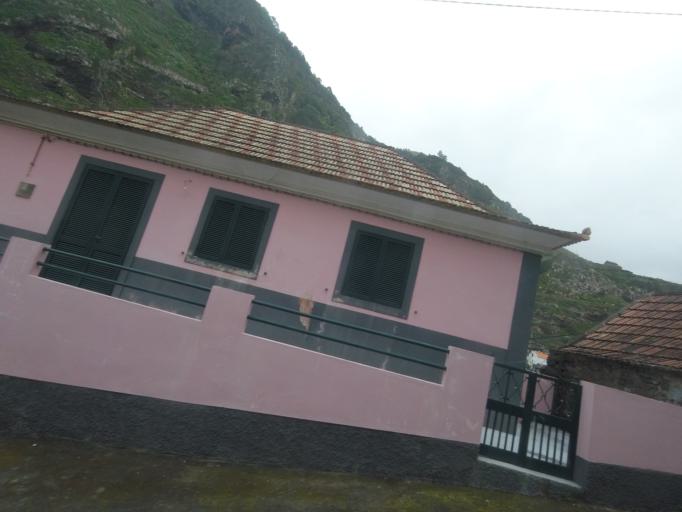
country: PT
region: Madeira
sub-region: Porto Moniz
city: Porto Moniz
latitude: 32.8546
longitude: -17.1547
